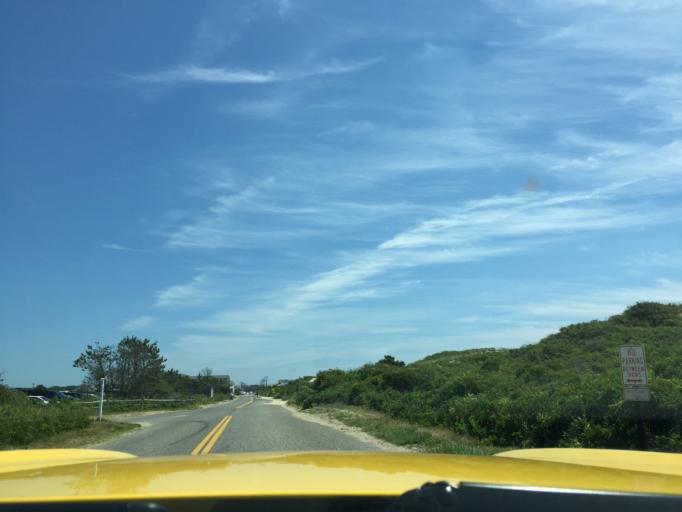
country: US
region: New York
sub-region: Suffolk County
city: Montauk
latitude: 41.0305
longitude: -71.9511
